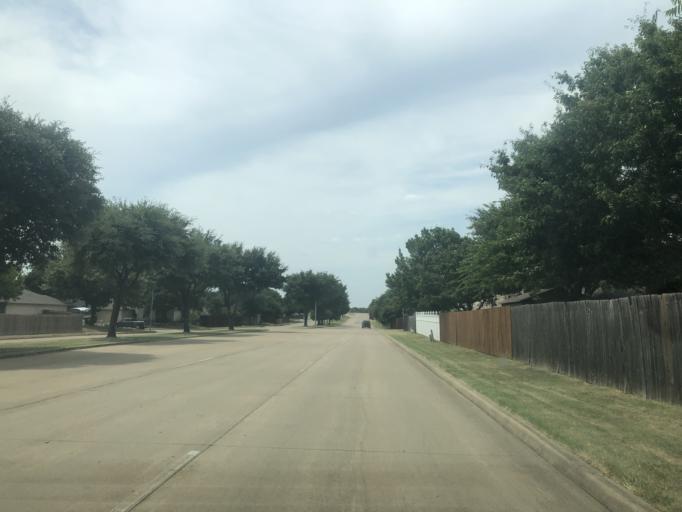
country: US
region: Texas
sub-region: Tarrant County
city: Blue Mound
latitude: 32.8736
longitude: -97.3485
